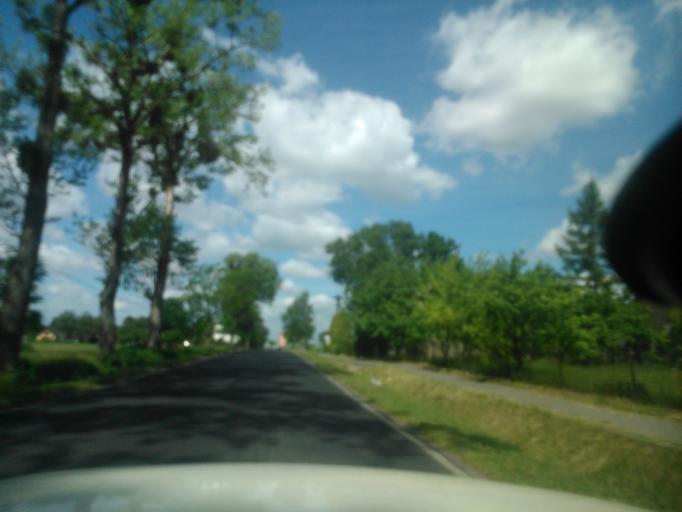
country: PL
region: Kujawsko-Pomorskie
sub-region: Powiat torunski
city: Obrowo
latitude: 53.0060
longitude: 18.8417
